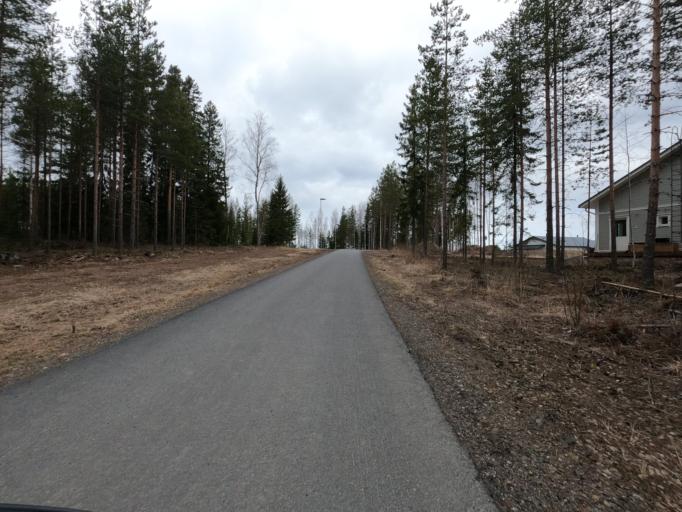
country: FI
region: North Karelia
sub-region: Joensuu
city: Joensuu
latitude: 62.5649
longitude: 29.8202
